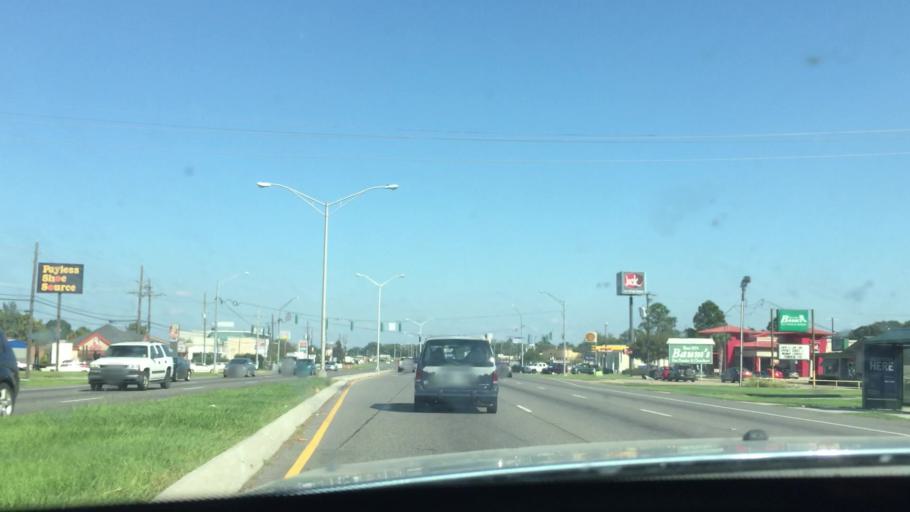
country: US
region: Louisiana
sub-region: East Baton Rouge Parish
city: Westminster
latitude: 30.4519
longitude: -91.1055
